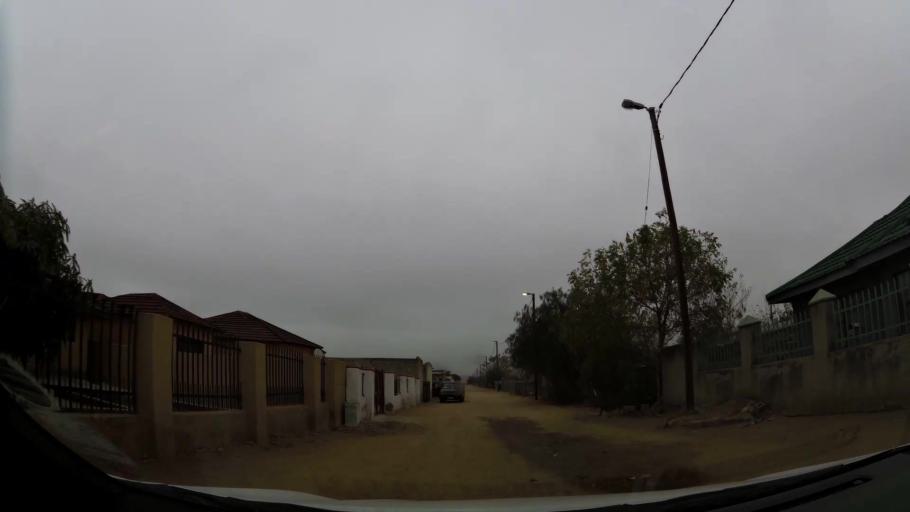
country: ZA
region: Limpopo
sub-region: Capricorn District Municipality
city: Polokwane
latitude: -23.8353
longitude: 29.3928
